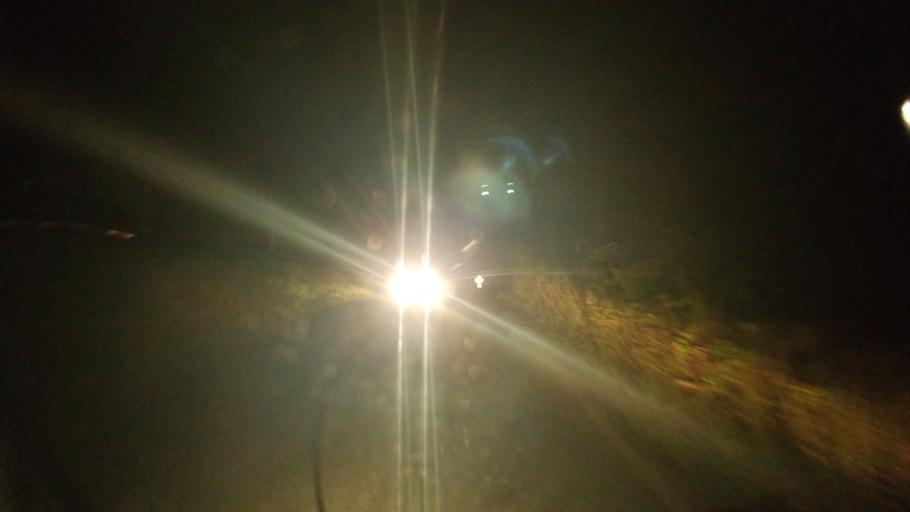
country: US
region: Ohio
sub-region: Hocking County
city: Logan
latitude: 39.5175
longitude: -82.4542
